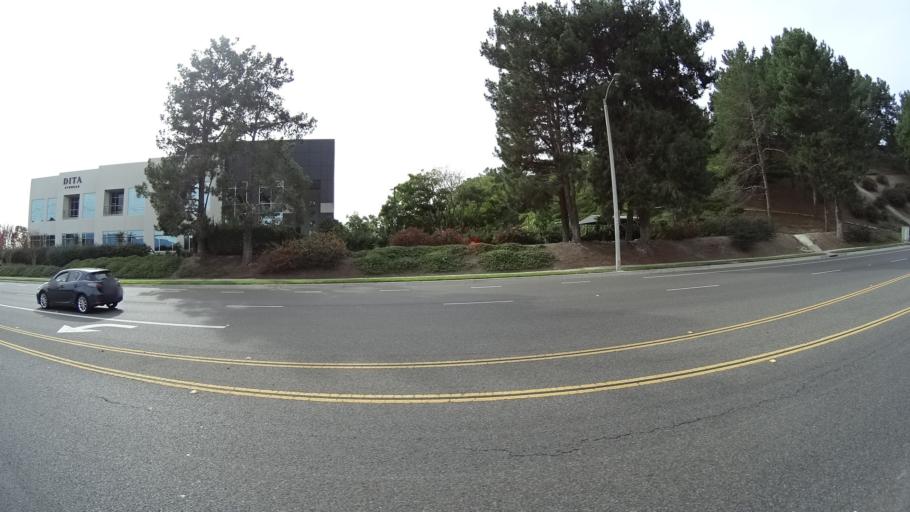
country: US
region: California
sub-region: Orange County
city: Laguna Woods
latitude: 33.5906
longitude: -117.7260
